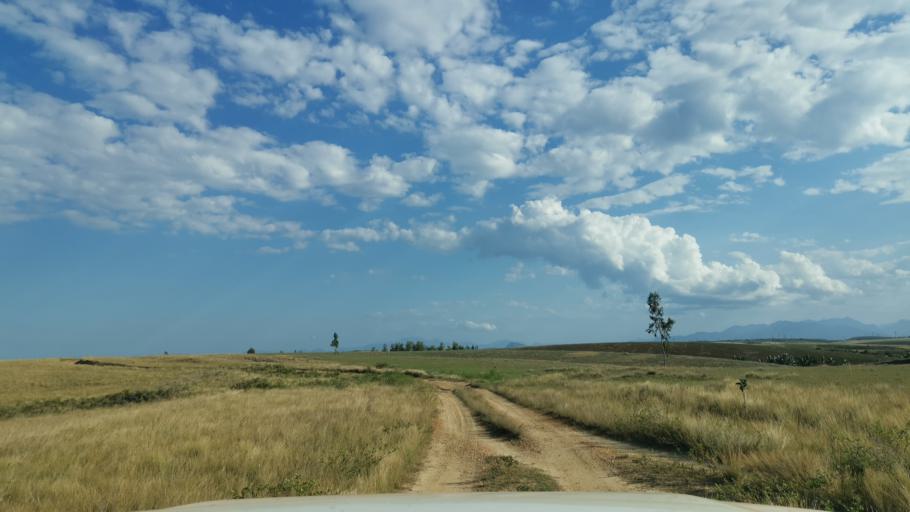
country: MG
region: Atsimo-Atsinanana
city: Vohipaho
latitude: -24.2068
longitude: 47.3480
